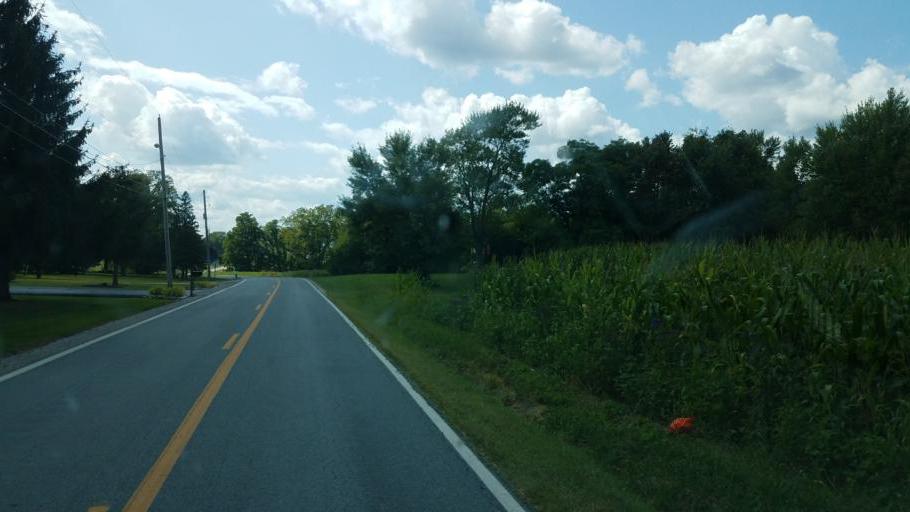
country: US
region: Ohio
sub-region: Delaware County
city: Lewis Center
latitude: 40.2258
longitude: -82.9867
